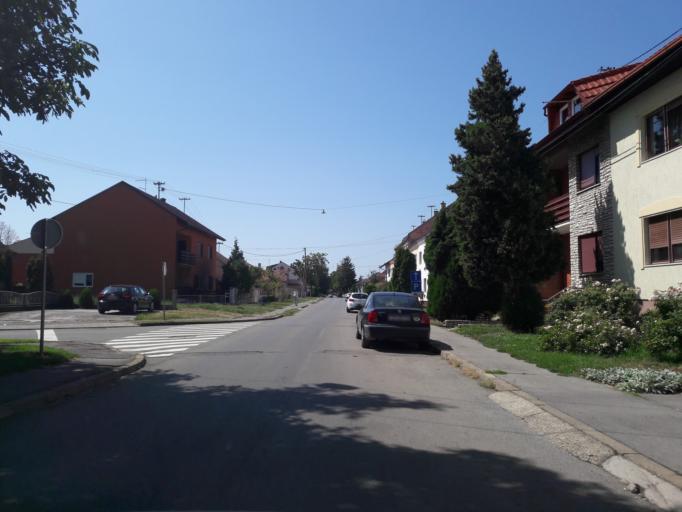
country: HR
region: Osjecko-Baranjska
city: Visnjevac
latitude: 45.5638
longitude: 18.6493
